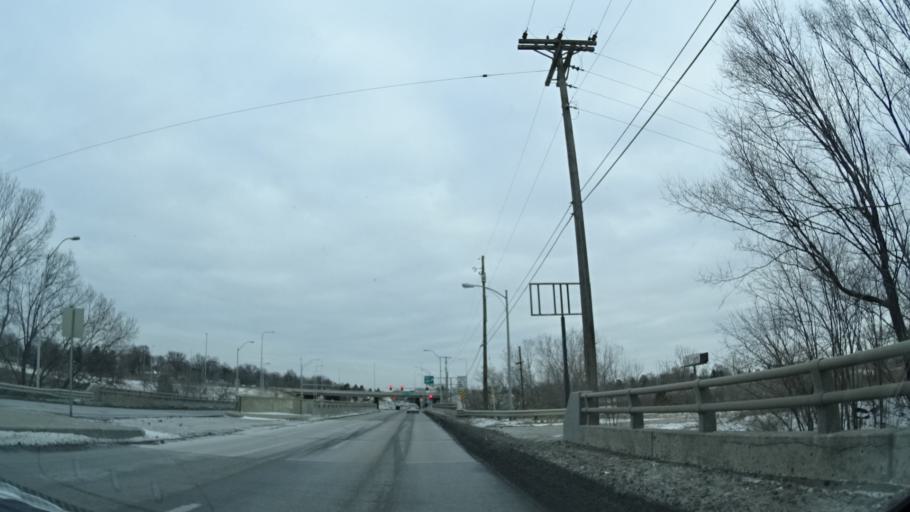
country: US
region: Nebraska
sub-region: Douglas County
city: Omaha
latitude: 41.2222
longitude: -95.9757
